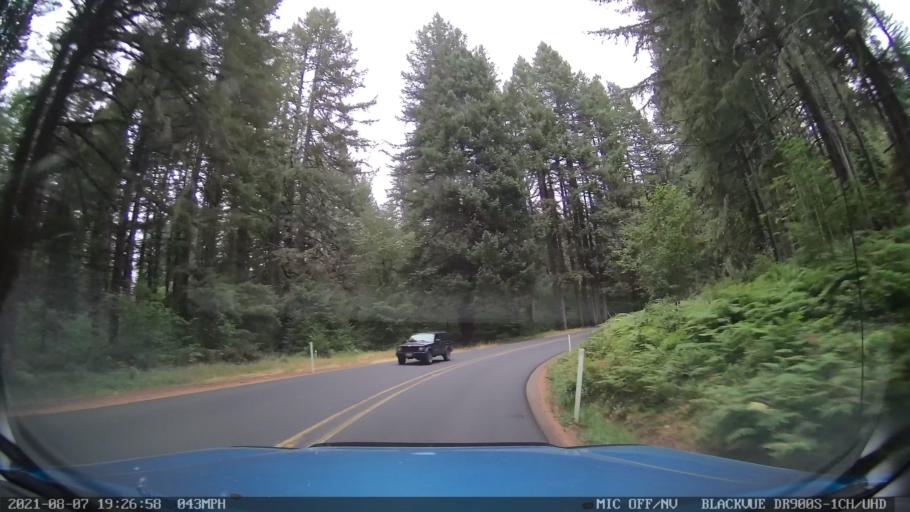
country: US
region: Oregon
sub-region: Linn County
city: Lyons
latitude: 44.8774
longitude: -122.6515
